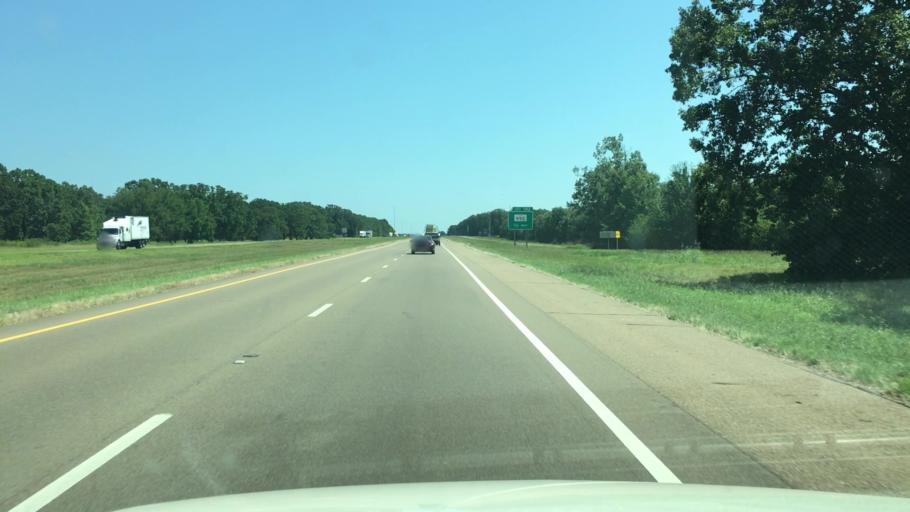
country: US
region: Texas
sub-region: Bowie County
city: De Kalb
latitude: 33.4041
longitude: -94.5729
